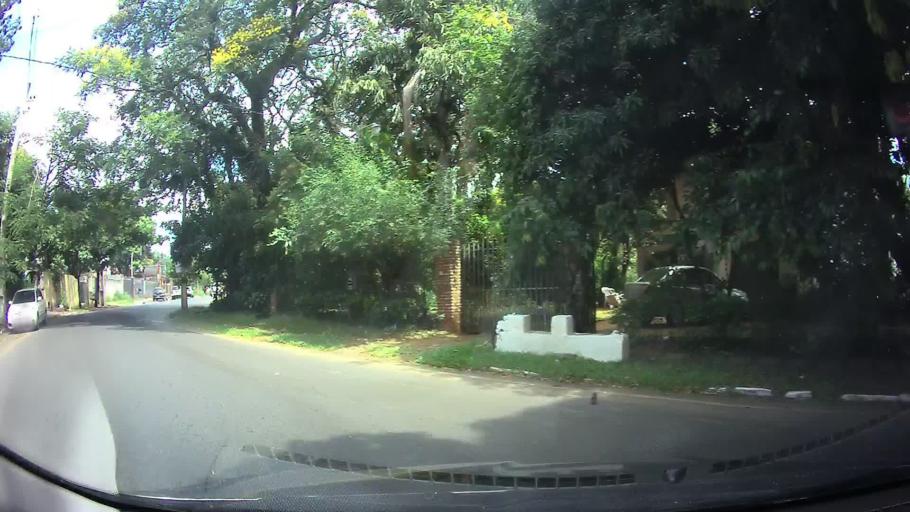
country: PY
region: Central
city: Fernando de la Mora
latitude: -25.3214
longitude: -57.5308
